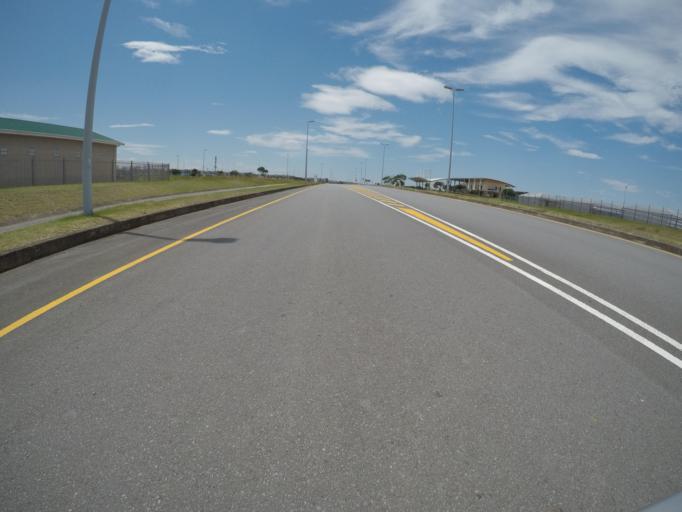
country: ZA
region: Eastern Cape
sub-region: Buffalo City Metropolitan Municipality
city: East London
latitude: -33.0519
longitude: 27.8468
